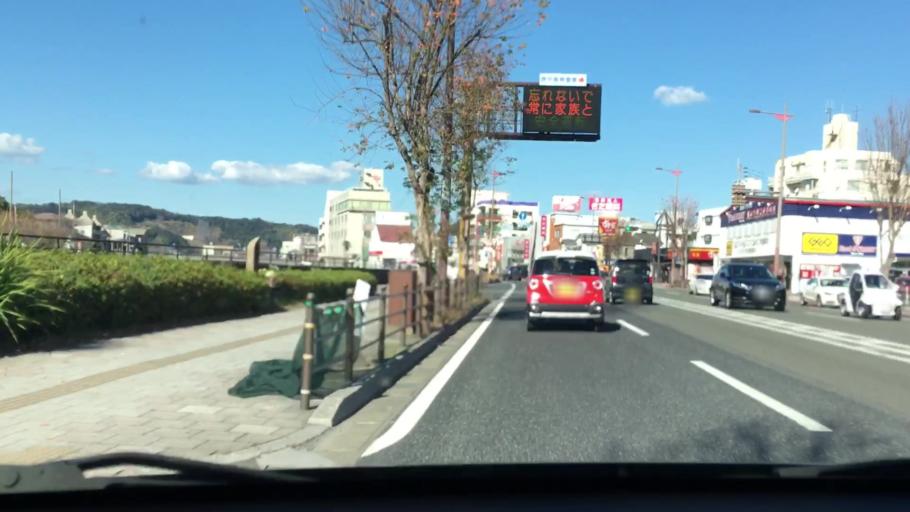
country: JP
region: Kagoshima
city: Kagoshima-shi
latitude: 31.6069
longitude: 130.5363
